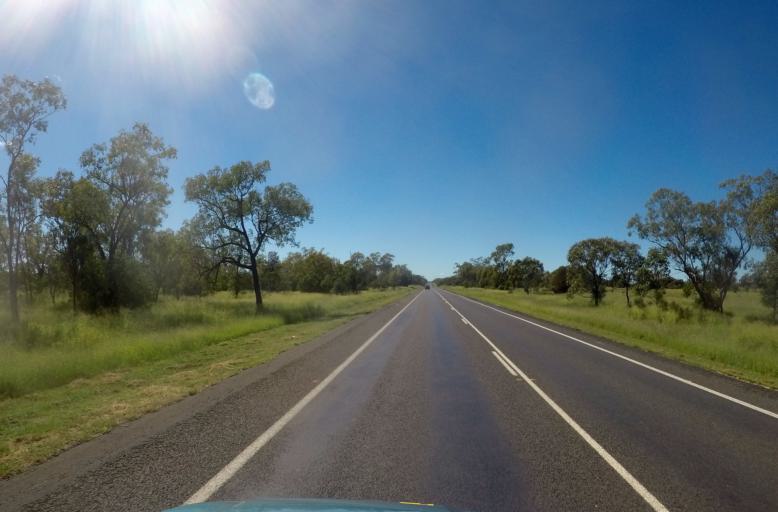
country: AU
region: Queensland
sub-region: Maranoa
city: Roma
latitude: -26.5860
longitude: 149.0171
